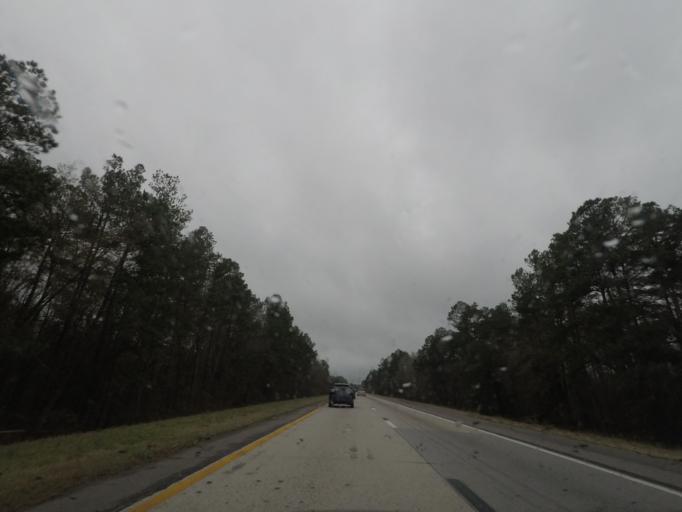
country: US
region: South Carolina
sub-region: Dorchester County
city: Saint George
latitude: 33.1070
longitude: -80.6446
